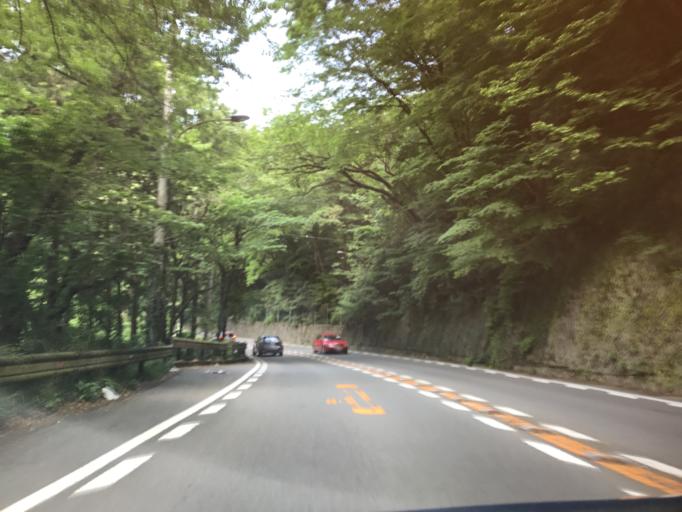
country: JP
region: Kanagawa
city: Hakone
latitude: 35.2330
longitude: 139.0840
